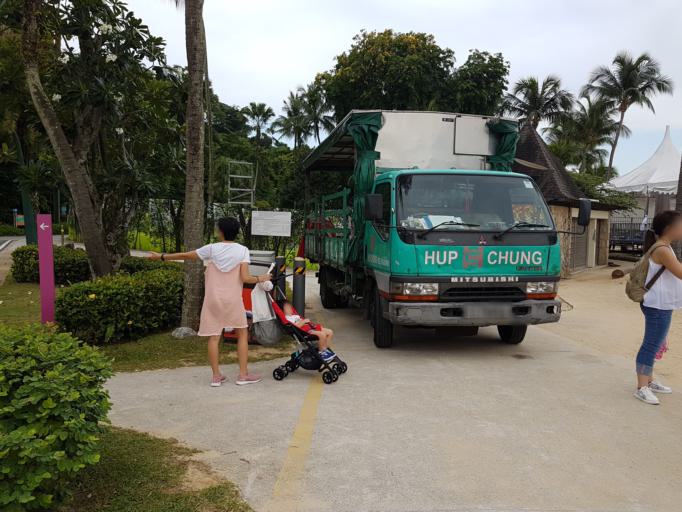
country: SG
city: Singapore
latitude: 1.2566
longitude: 103.8119
